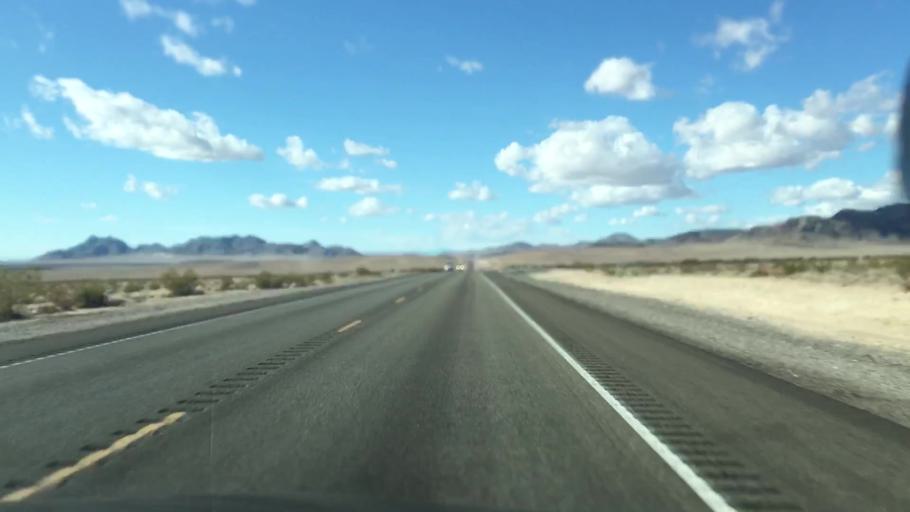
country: US
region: Nevada
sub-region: Nye County
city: Pahrump
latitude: 36.6024
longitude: -116.2512
